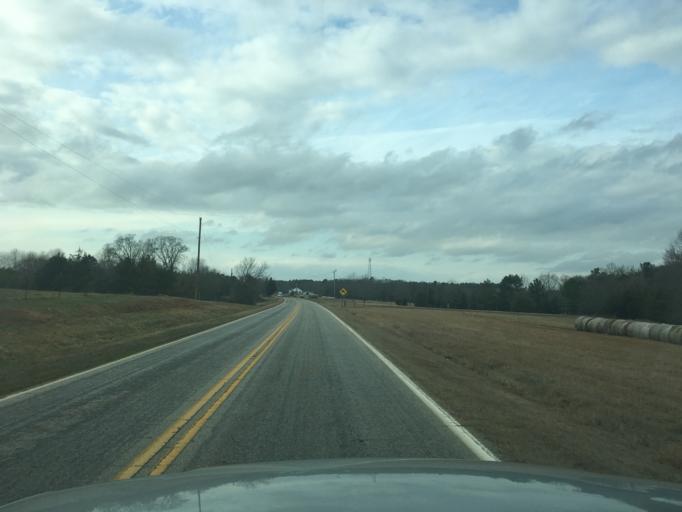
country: US
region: South Carolina
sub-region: Abbeville County
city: Due West
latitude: 34.3189
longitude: -82.4654
